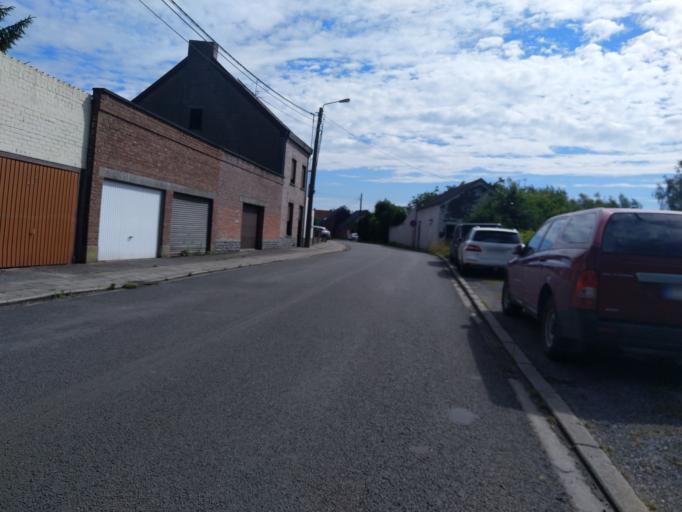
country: BE
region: Wallonia
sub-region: Province du Hainaut
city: Quievrain
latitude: 50.4113
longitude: 3.6884
